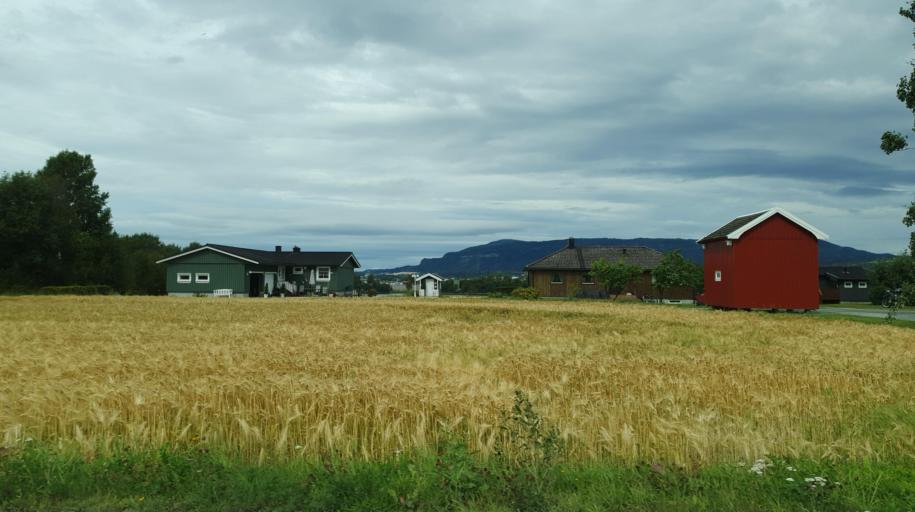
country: NO
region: Nord-Trondelag
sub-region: Stjordal
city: Stjordalshalsen
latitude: 63.4446
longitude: 10.9393
